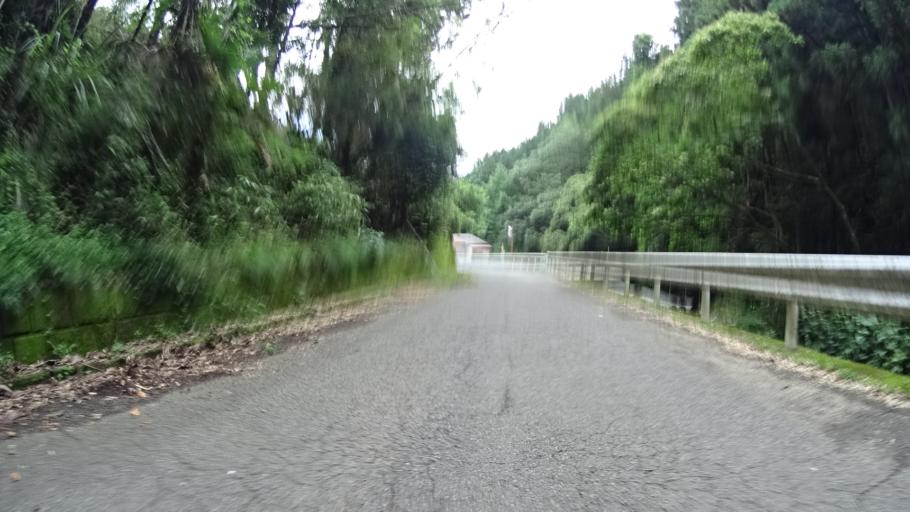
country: JP
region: Kanagawa
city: Atsugi
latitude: 35.4981
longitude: 139.2667
